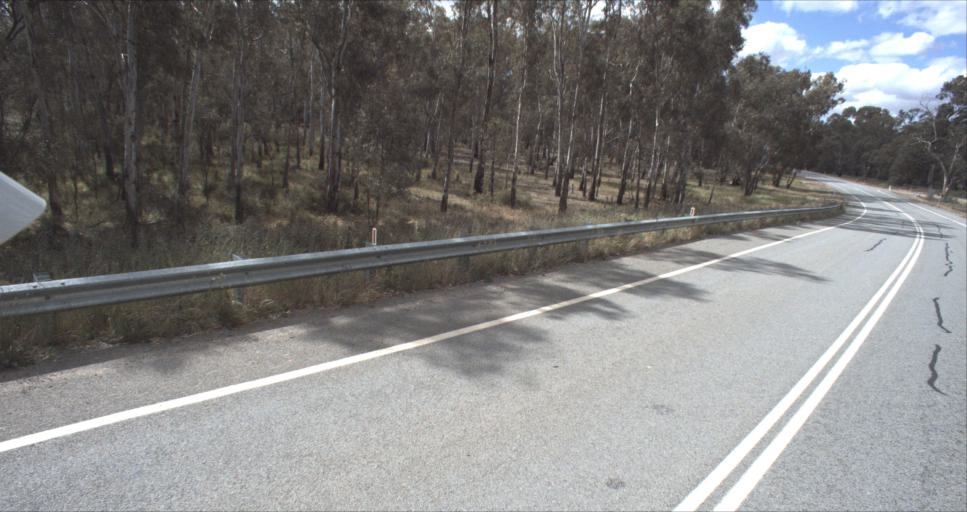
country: AU
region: New South Wales
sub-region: Leeton
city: Leeton
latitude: -34.6383
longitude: 146.3744
